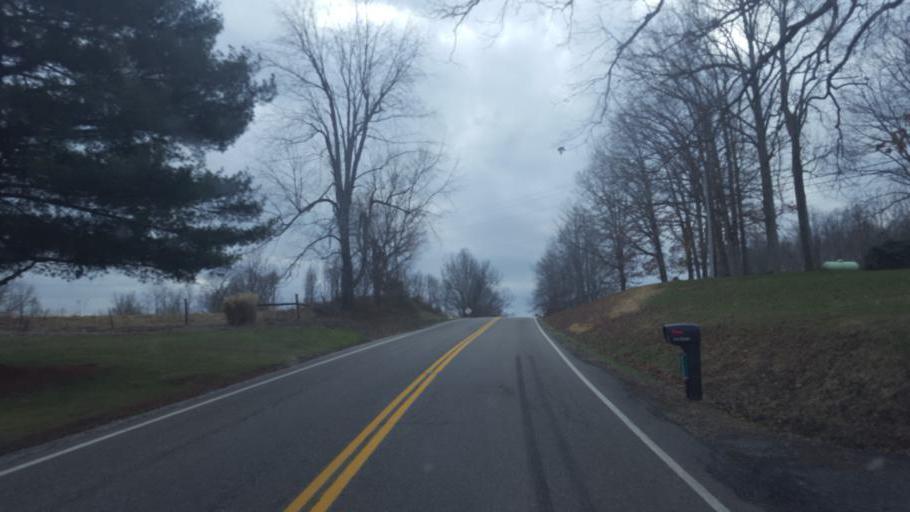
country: US
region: Ohio
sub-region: Jackson County
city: Oak Hill
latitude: 38.8044
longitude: -82.3991
